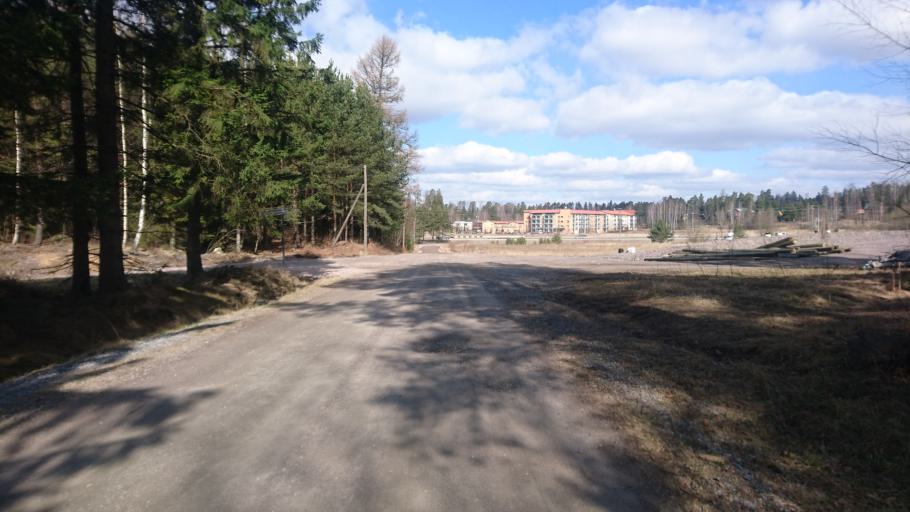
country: FI
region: Uusimaa
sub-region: Helsinki
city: Kauniainen
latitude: 60.1944
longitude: 24.7366
